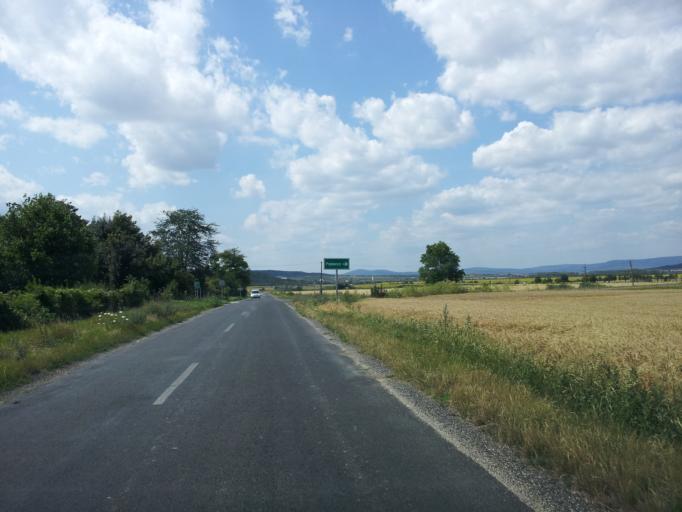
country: HU
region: Veszprem
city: Balatonkenese
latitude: 47.0721
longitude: 18.0708
